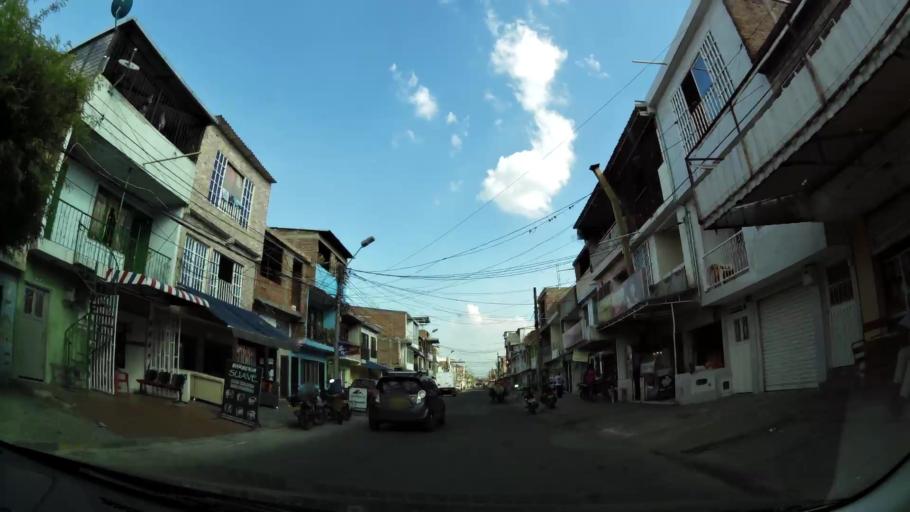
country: CO
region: Valle del Cauca
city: Cali
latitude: 3.4178
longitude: -76.4993
